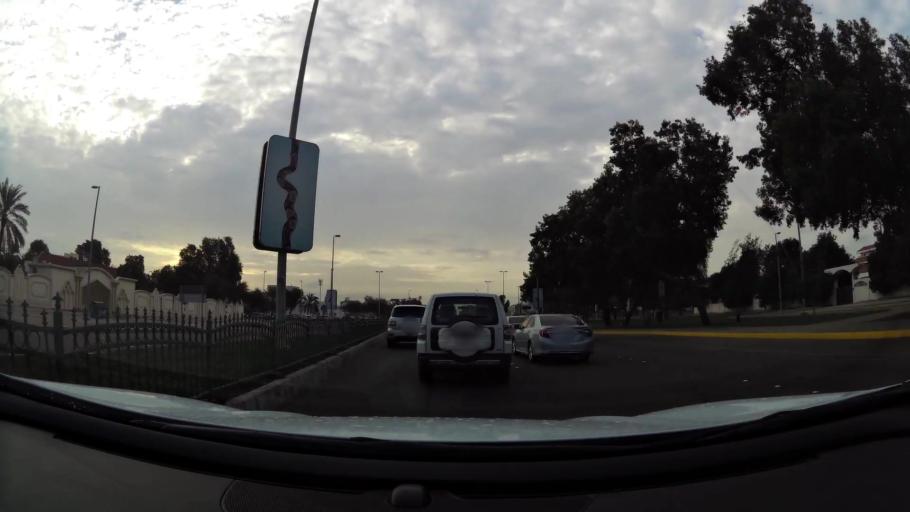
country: AE
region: Abu Dhabi
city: Abu Dhabi
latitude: 24.4460
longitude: 54.3655
